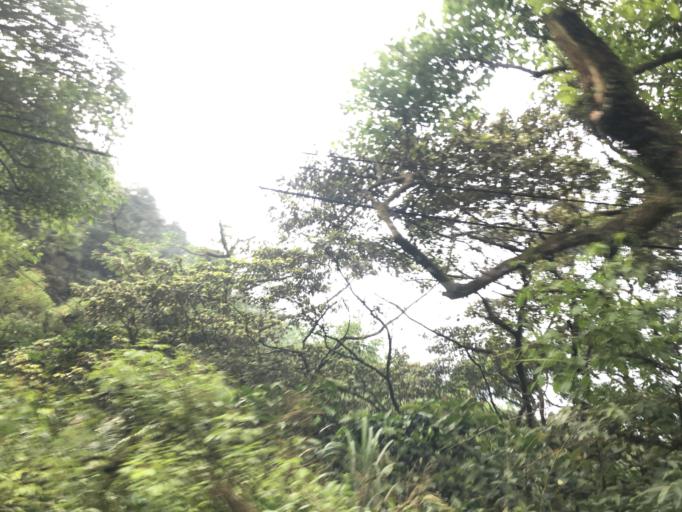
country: TW
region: Taiwan
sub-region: Keelung
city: Keelung
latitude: 25.1491
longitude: 121.6254
